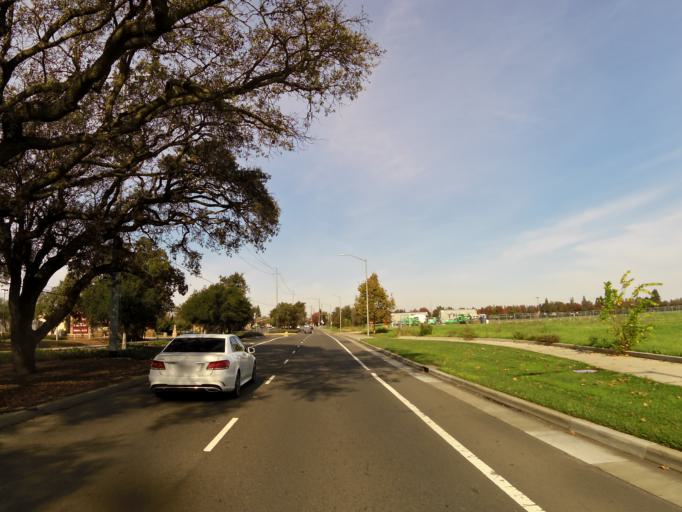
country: US
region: California
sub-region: Sacramento County
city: Laguna
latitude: 38.4058
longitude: -121.4175
